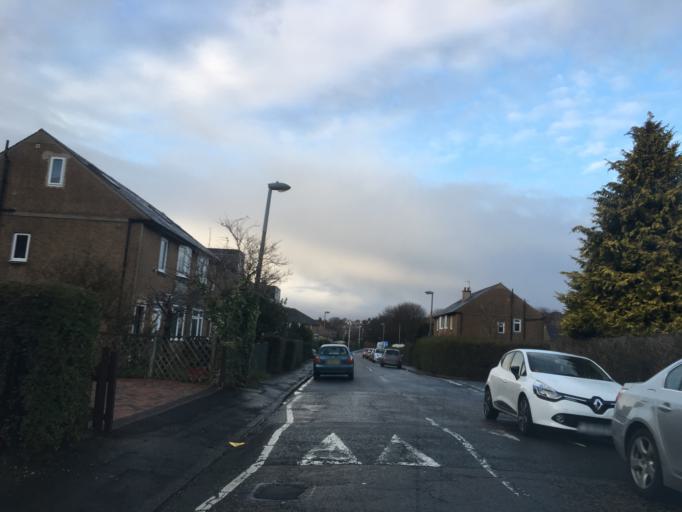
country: GB
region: Scotland
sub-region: Edinburgh
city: Colinton
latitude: 55.9358
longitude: -3.2732
